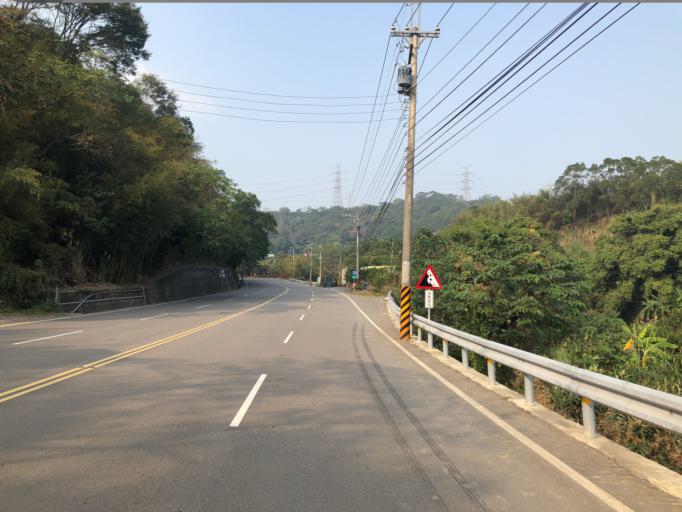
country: TW
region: Taiwan
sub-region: Miaoli
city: Miaoli
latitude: 24.6118
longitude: 120.9585
